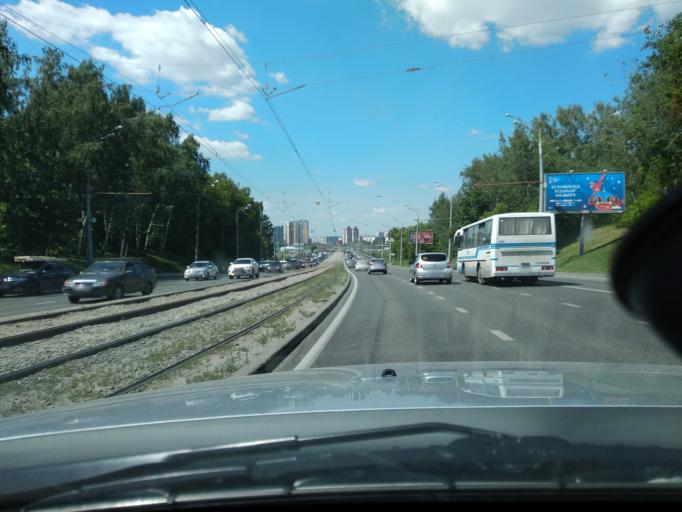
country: RU
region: Tatarstan
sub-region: Gorod Kazan'
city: Kazan
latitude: 55.8204
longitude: 49.1740
